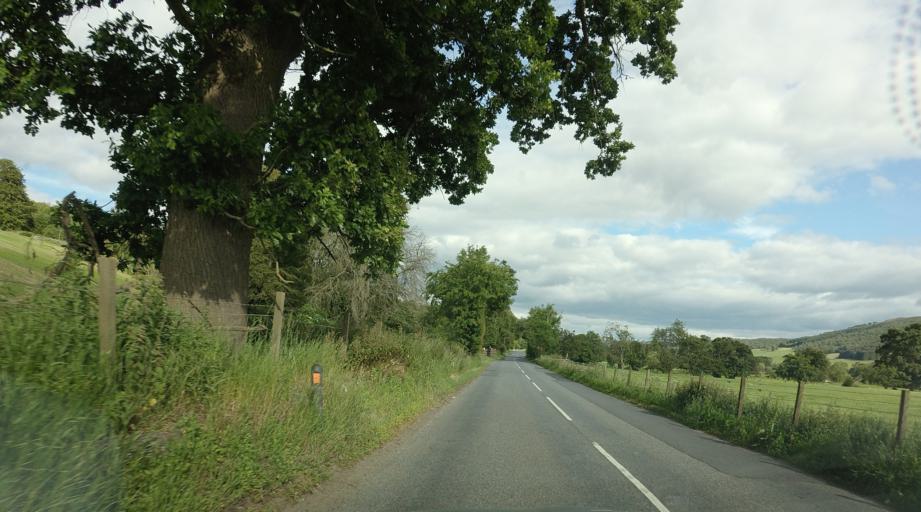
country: GB
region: Scotland
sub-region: Perth and Kinross
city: Pitlochry
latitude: 56.6550
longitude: -3.7194
